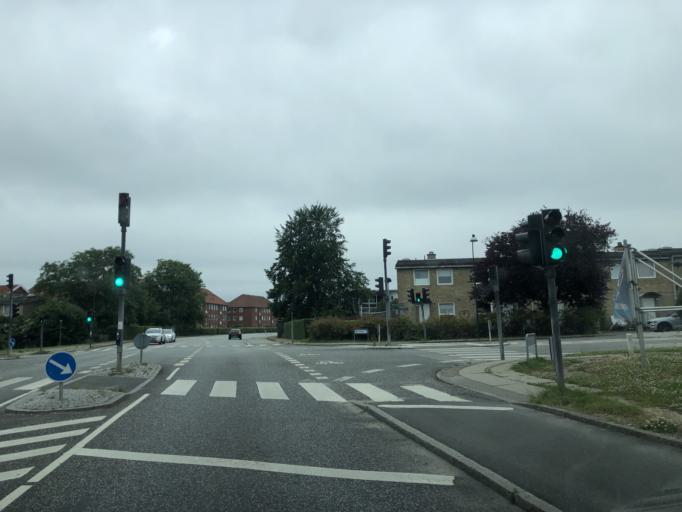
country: DK
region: Capital Region
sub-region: Rudersdal Kommune
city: Trorod
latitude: 55.8166
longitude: 12.5383
